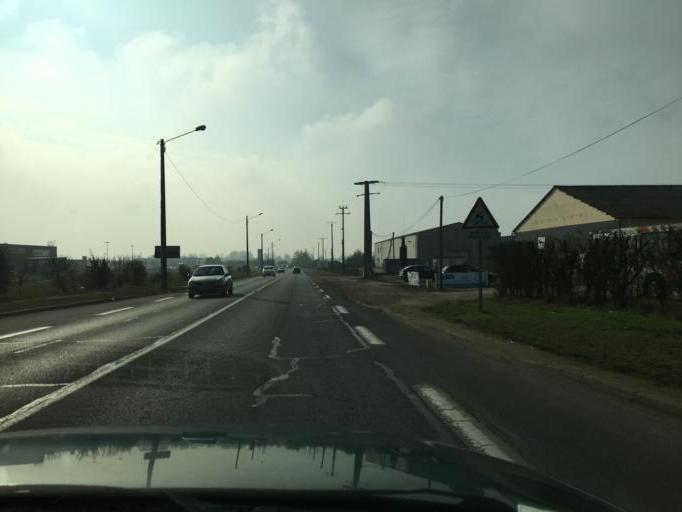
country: FR
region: Centre
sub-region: Departement du Loiret
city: Tavers
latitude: 47.7691
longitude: 1.6145
